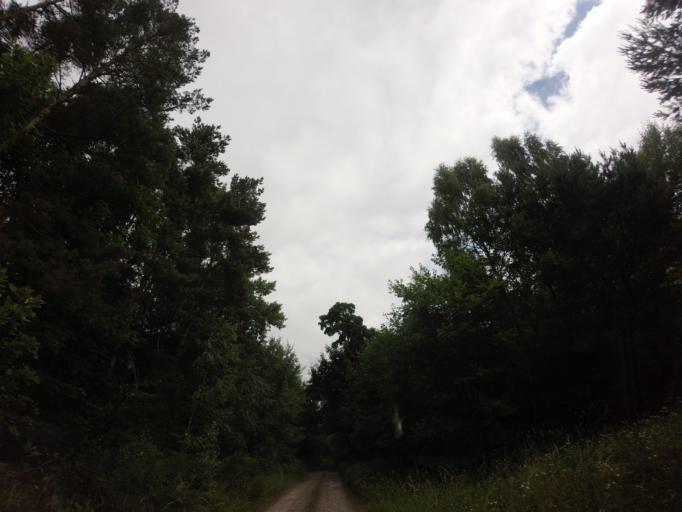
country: PL
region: West Pomeranian Voivodeship
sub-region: Powiat choszczenski
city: Krzecin
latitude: 53.0223
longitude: 15.5320
